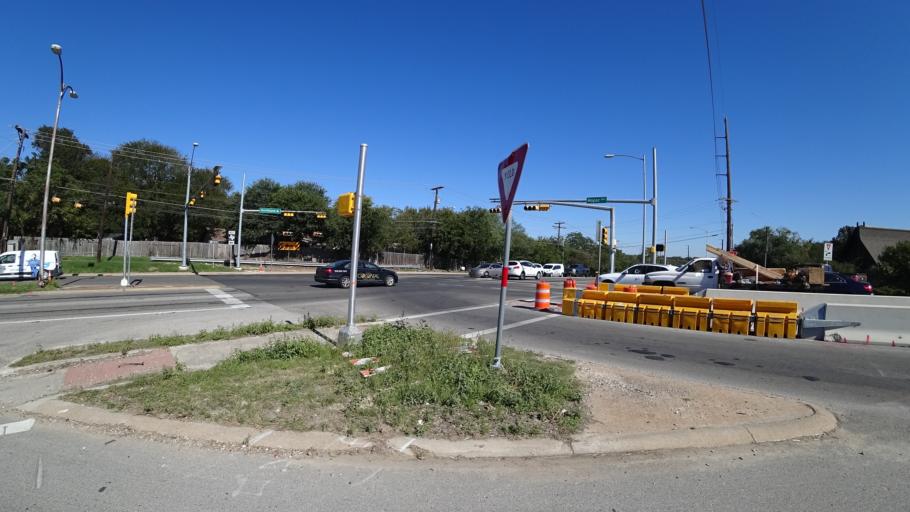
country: US
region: Texas
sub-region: Travis County
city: West Lake Hills
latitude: 30.3354
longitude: -97.7540
